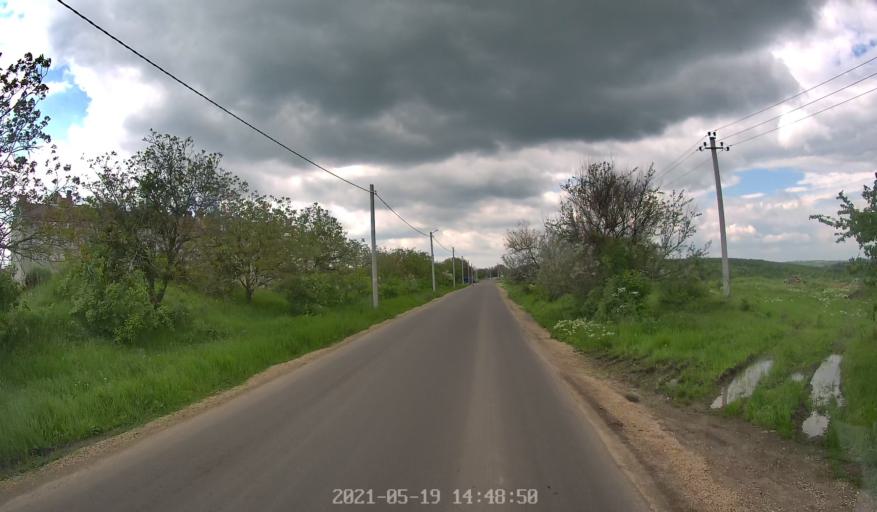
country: MD
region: Chisinau
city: Stauceni
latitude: 47.0464
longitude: 28.9572
